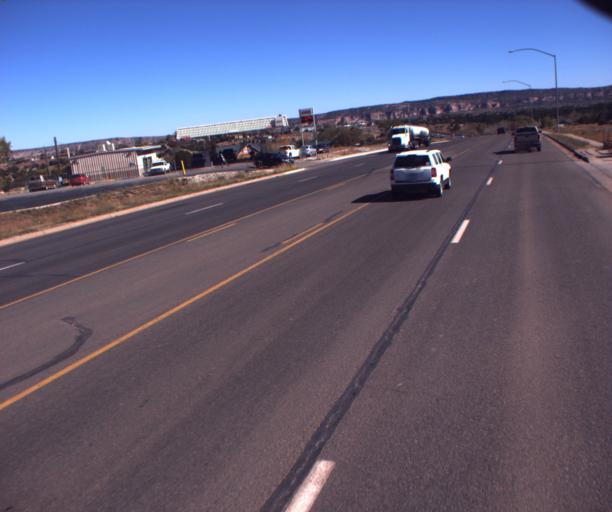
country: US
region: Arizona
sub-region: Apache County
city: Saint Michaels
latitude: 35.6566
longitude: -109.1092
